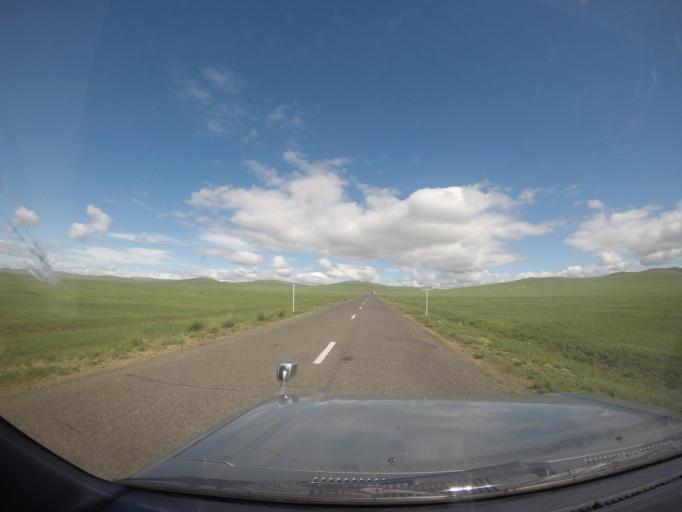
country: MN
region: Hentiy
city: Avraga
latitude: 47.4814
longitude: 109.5046
